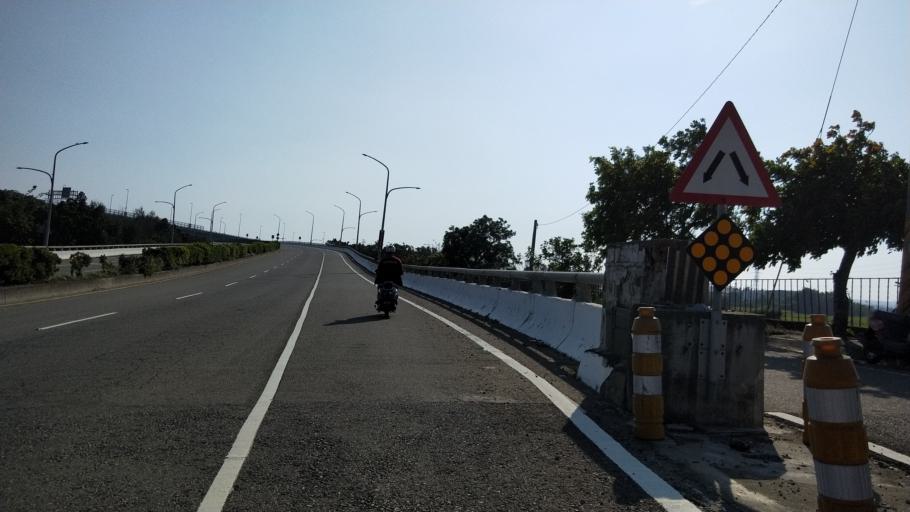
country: TW
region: Taiwan
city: Fengyuan
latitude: 24.3087
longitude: 120.5985
